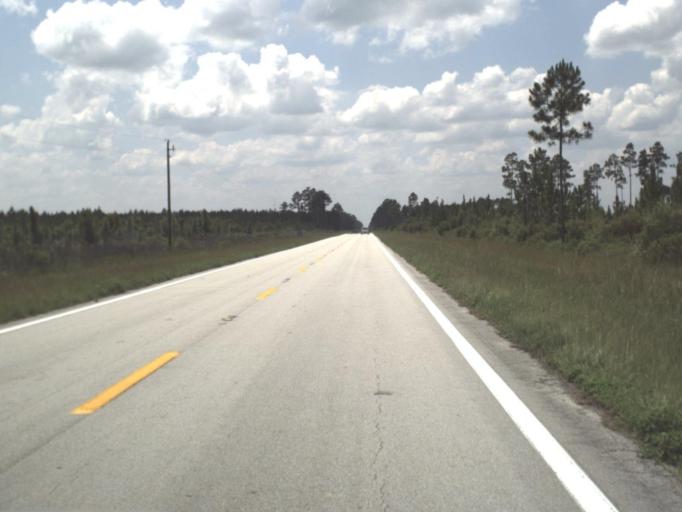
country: US
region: Florida
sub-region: Baker County
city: Macclenny
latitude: 30.5371
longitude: -82.3271
